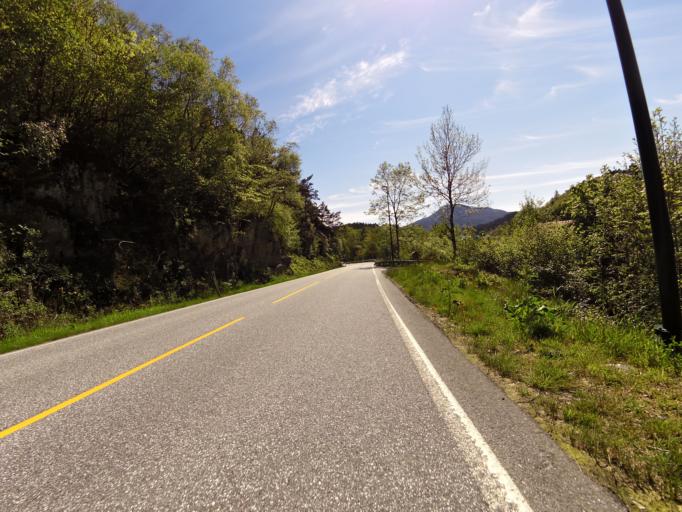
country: NO
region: Hordaland
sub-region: Stord
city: Sagvag
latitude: 59.7909
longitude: 5.3731
